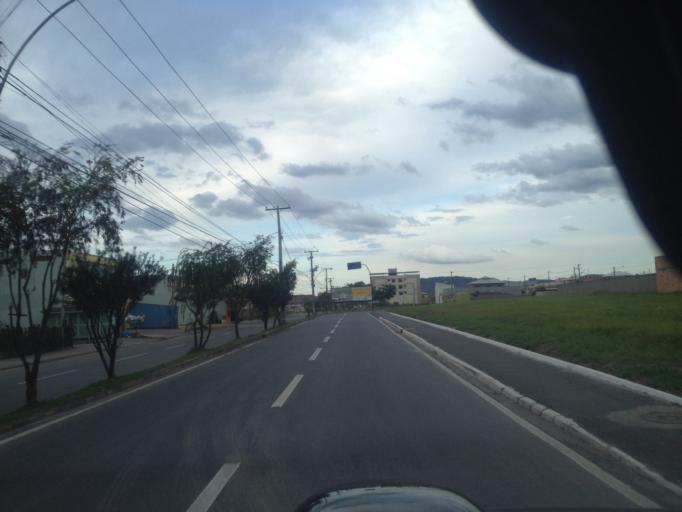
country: BR
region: Rio de Janeiro
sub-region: Porto Real
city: Porto Real
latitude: -22.4136
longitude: -44.3122
